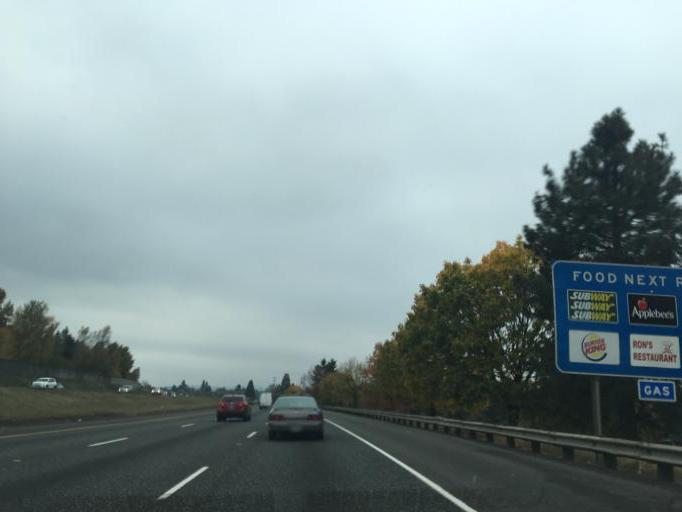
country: US
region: Oregon
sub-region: Multnomah County
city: Lents
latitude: 45.4635
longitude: -122.5697
